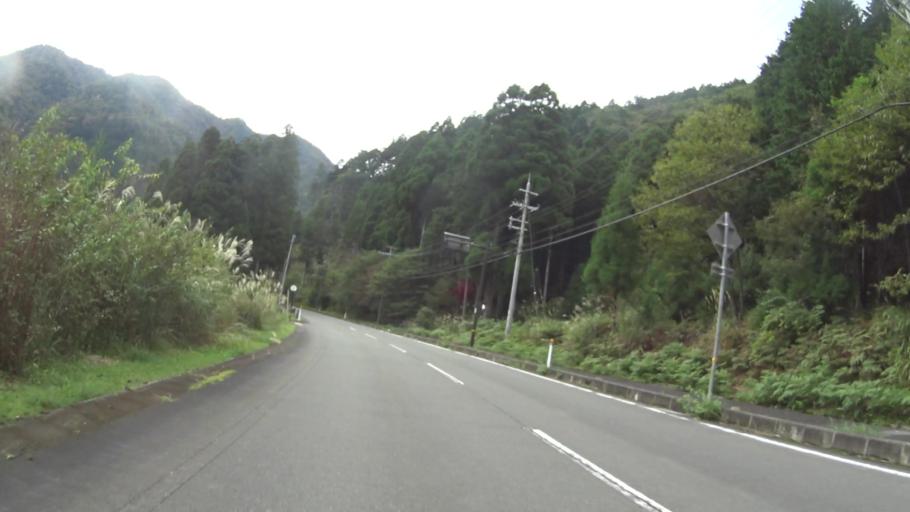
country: JP
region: Fukui
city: Obama
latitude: 35.3241
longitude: 135.6689
